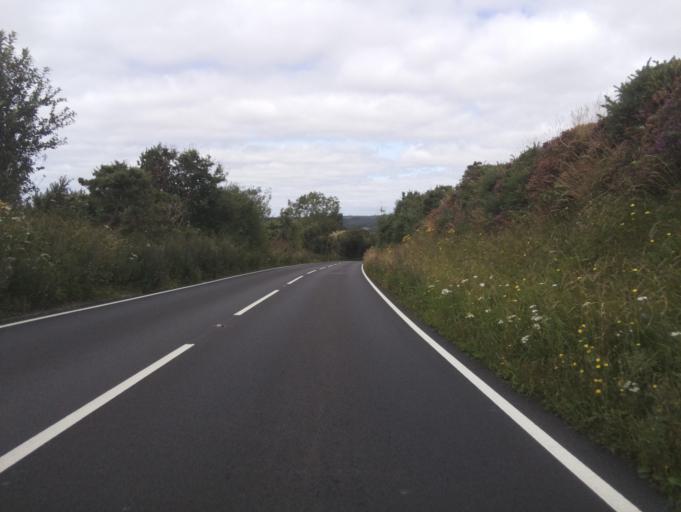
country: GB
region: England
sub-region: Devon
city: Bishopsteignton
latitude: 50.5822
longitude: -3.5322
